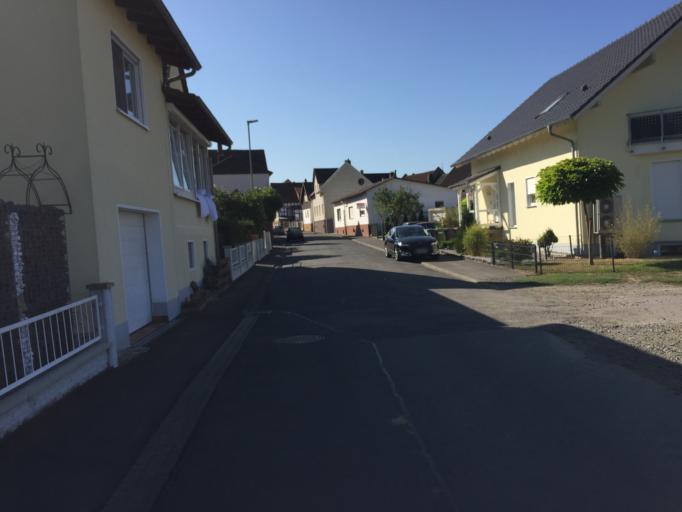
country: DE
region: Hesse
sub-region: Regierungsbezirk Darmstadt
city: Nidda
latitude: 50.4343
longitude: 8.9753
